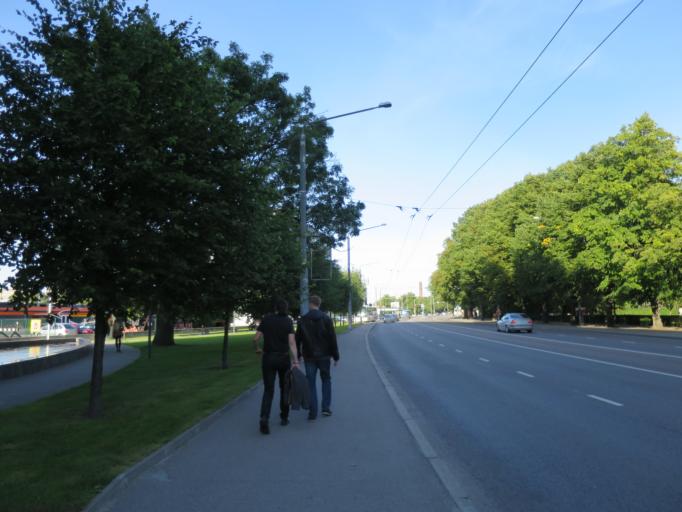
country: EE
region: Harju
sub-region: Tallinna linn
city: Tallinn
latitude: 59.4387
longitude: 24.7349
